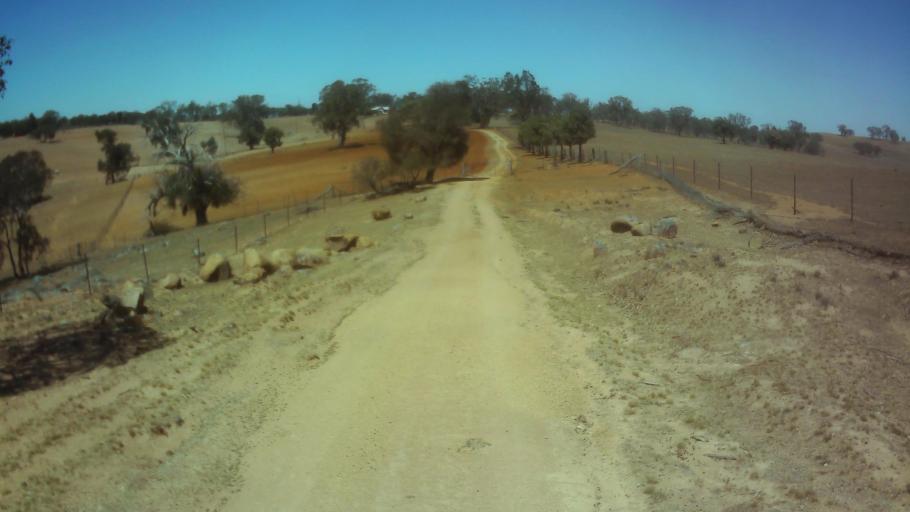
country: AU
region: New South Wales
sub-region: Cowra
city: Cowra
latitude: -33.9056
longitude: 148.5087
